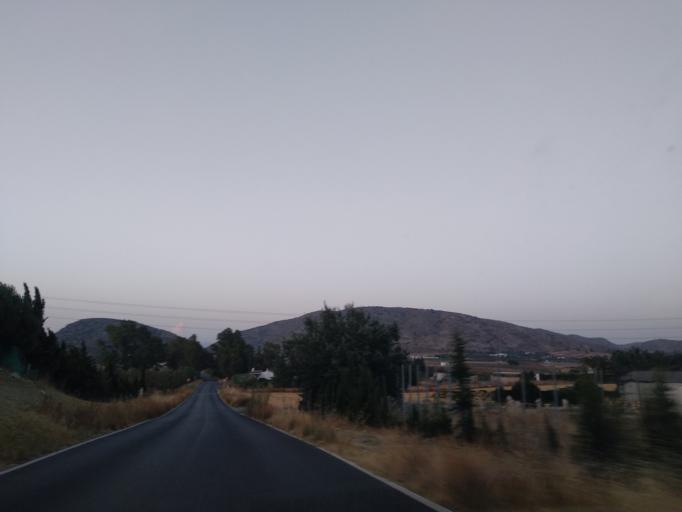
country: ES
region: Andalusia
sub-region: Provincia de Malaga
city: Cartama
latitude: 36.6801
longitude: -4.6572
